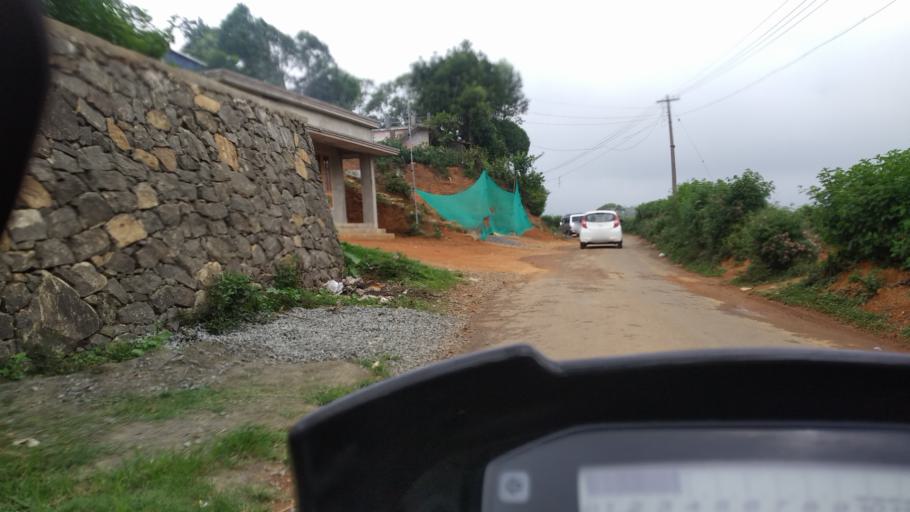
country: IN
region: Kerala
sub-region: Kottayam
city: Erattupetta
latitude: 9.5852
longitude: 77.0098
